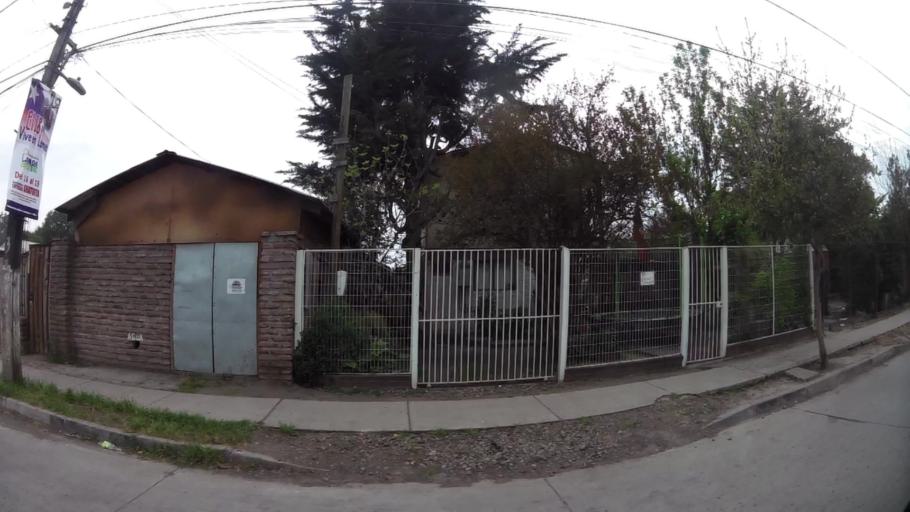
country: CL
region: Santiago Metropolitan
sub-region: Provincia de Chacabuco
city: Lampa
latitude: -33.2265
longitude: -70.8091
